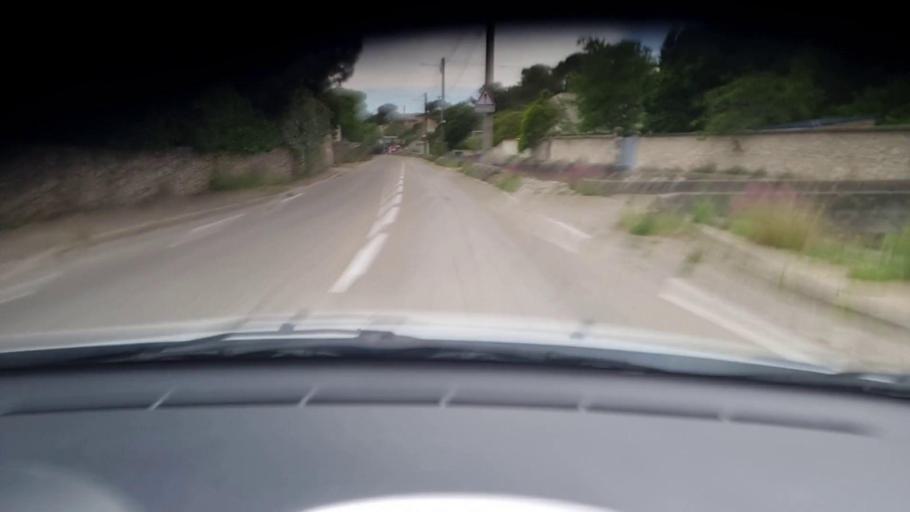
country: FR
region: Languedoc-Roussillon
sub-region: Departement du Gard
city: Nimes
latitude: 43.8584
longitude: 4.3781
